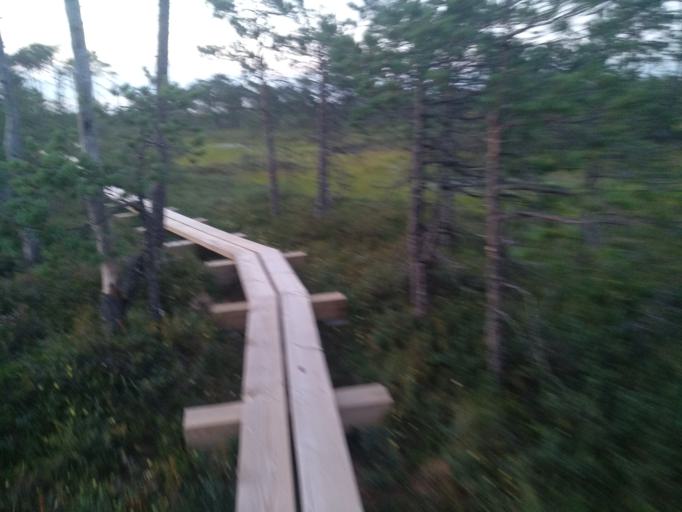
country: EE
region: Jaervamaa
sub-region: Paide linn
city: Paide
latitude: 59.0747
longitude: 25.5237
